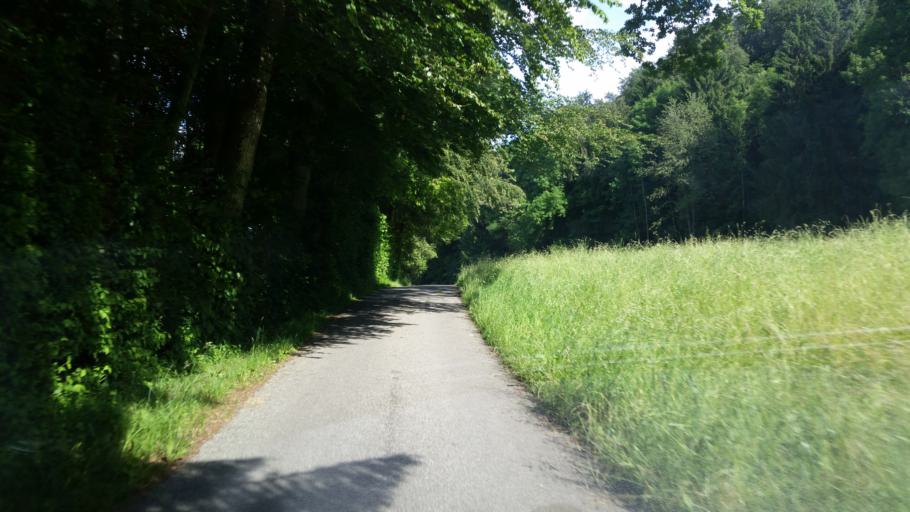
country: CH
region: Aargau
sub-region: Bezirk Bremgarten
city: Rudolfstetten
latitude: 47.3864
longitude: 8.3816
